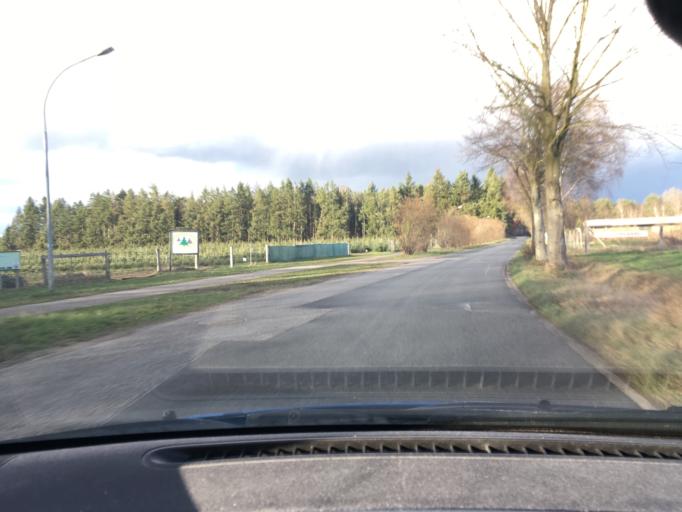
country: DE
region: Lower Saxony
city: Asendorf
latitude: 53.2997
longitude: 9.9840
